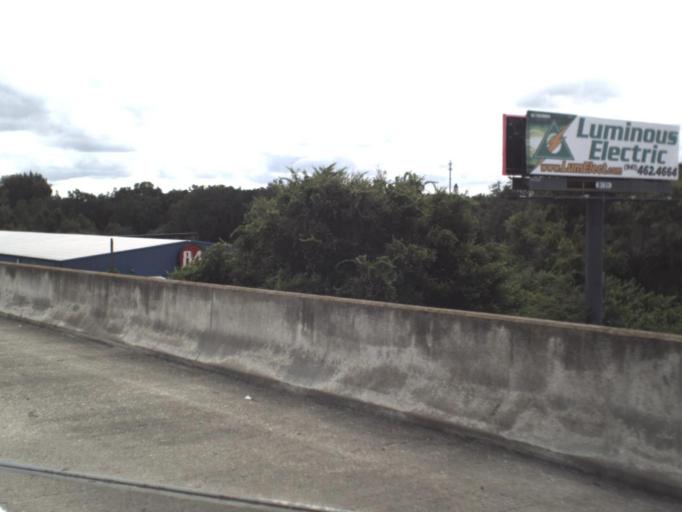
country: US
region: Florida
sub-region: Manatee County
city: West Samoset
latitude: 27.4770
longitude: -82.5500
